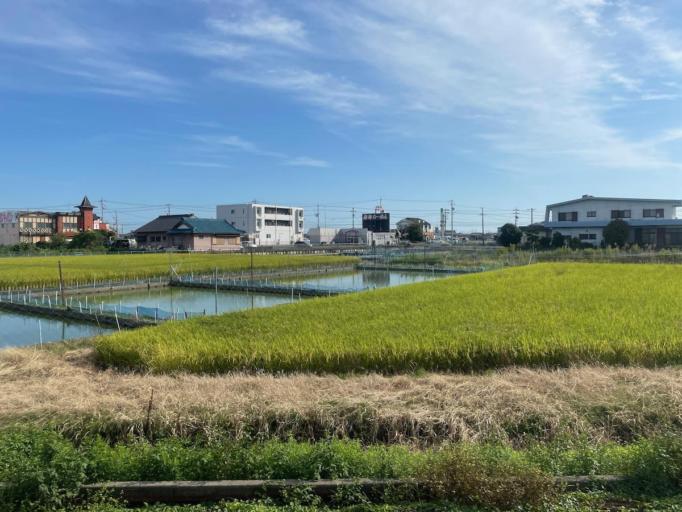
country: JP
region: Aichi
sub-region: Aisai-shi
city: Aisai
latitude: 35.1151
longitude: 136.7341
